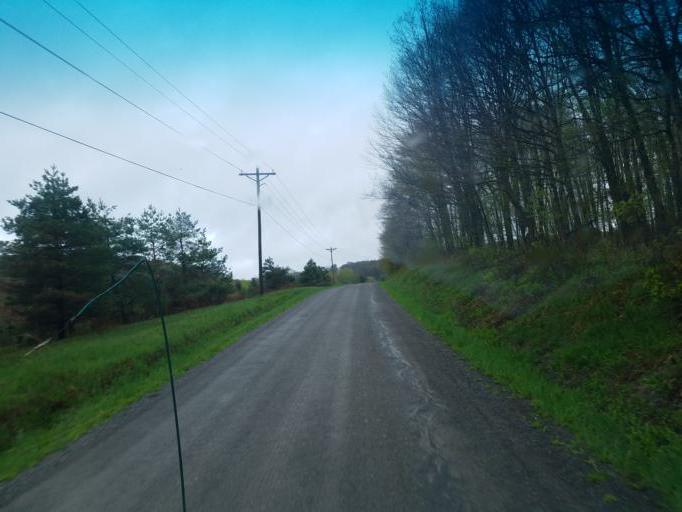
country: US
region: Pennsylvania
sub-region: Tioga County
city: Westfield
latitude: 41.9810
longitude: -77.6900
